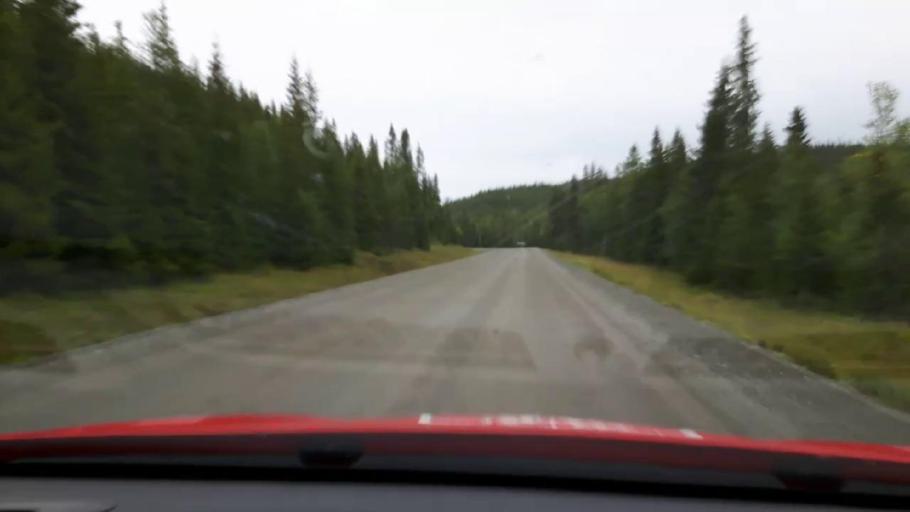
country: SE
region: Jaemtland
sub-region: Are Kommun
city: Are
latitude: 63.4248
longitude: 12.7409
